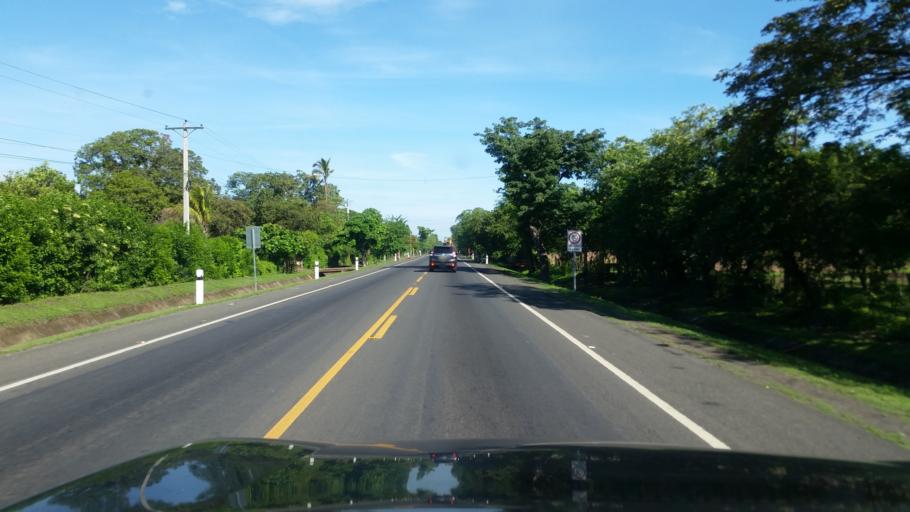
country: NI
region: Leon
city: Telica
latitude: 12.5247
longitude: -86.8756
